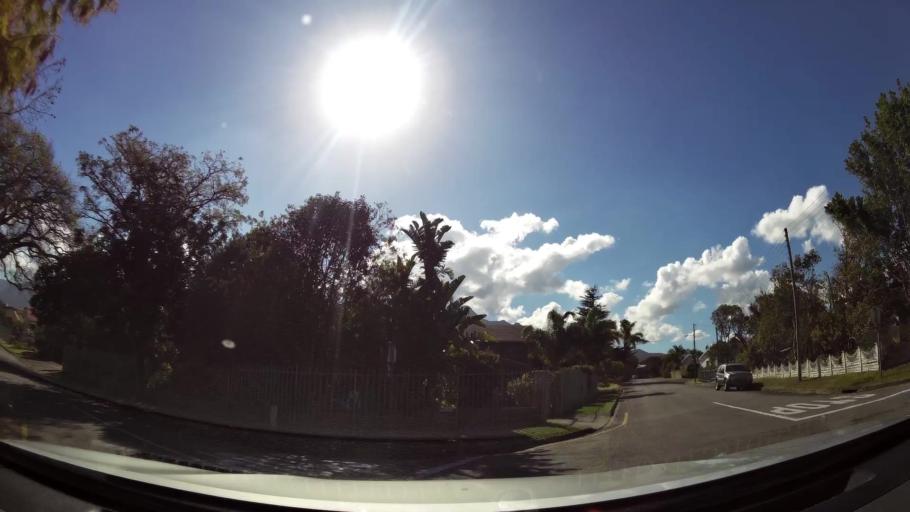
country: ZA
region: Western Cape
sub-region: Eden District Municipality
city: George
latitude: -33.9625
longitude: 22.4503
